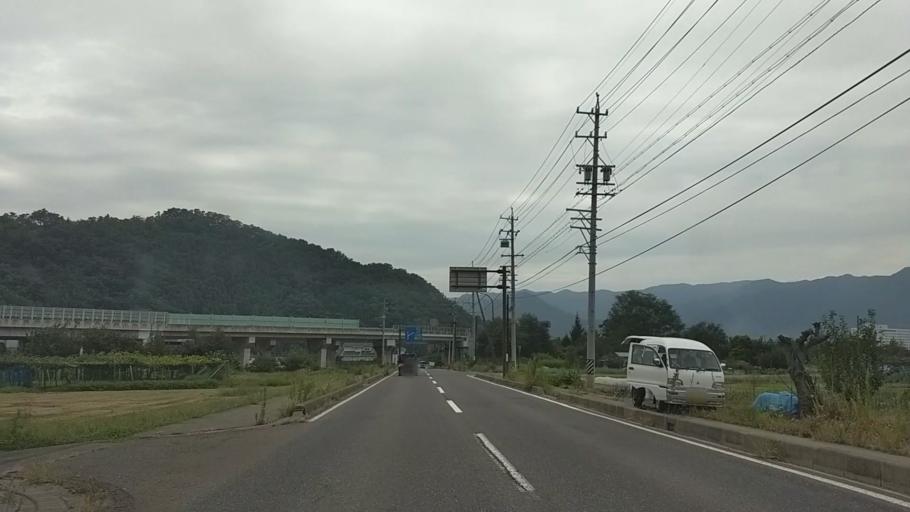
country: JP
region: Nagano
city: Nagano-shi
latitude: 36.5802
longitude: 138.2023
